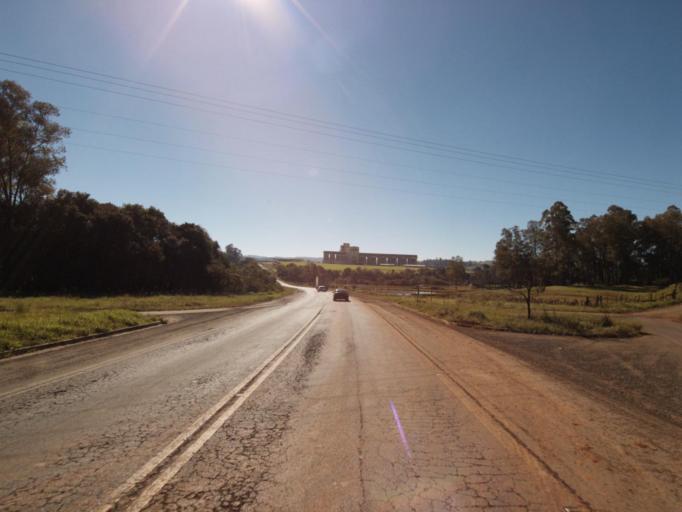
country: BR
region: Rio Grande do Sul
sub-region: Frederico Westphalen
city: Frederico Westphalen
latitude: -26.9138
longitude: -53.1882
